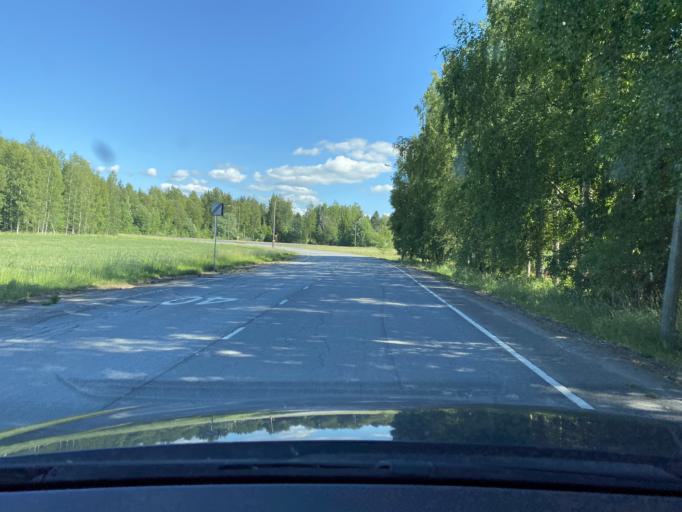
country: FI
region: Satakunta
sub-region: Pori
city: Huittinen
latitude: 61.1763
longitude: 22.7089
